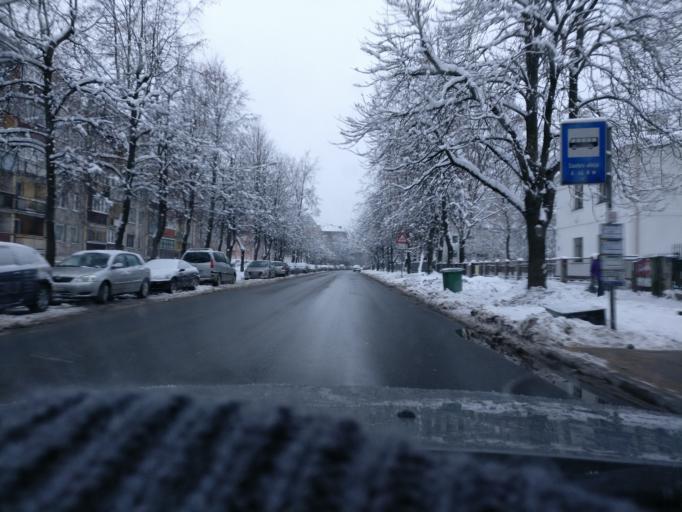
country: LV
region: Marupe
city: Marupe
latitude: 56.9302
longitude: 24.0744
